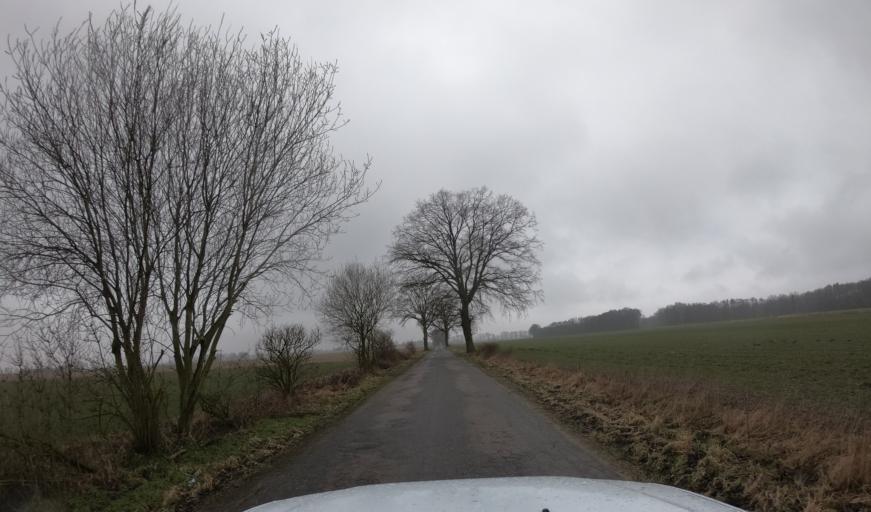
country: PL
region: West Pomeranian Voivodeship
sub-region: Powiat kamienski
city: Kamien Pomorski
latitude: 53.9034
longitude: 14.8221
